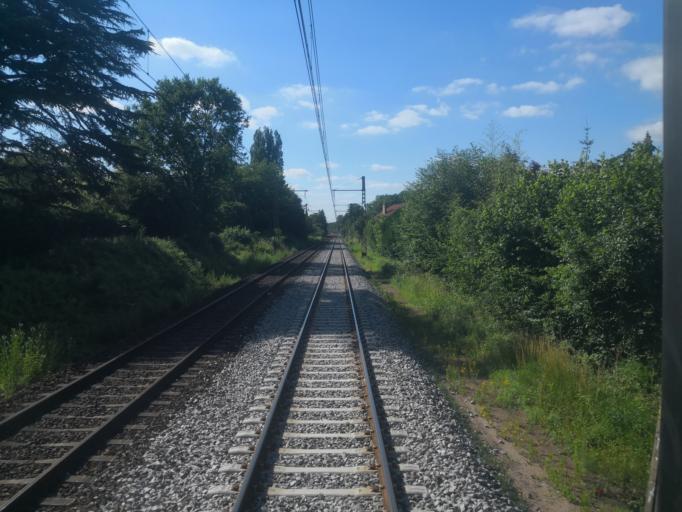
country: FR
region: Ile-de-France
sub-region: Departement de Seine-et-Marne
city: Bois-le-Roi
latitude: 48.4730
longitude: 2.6960
